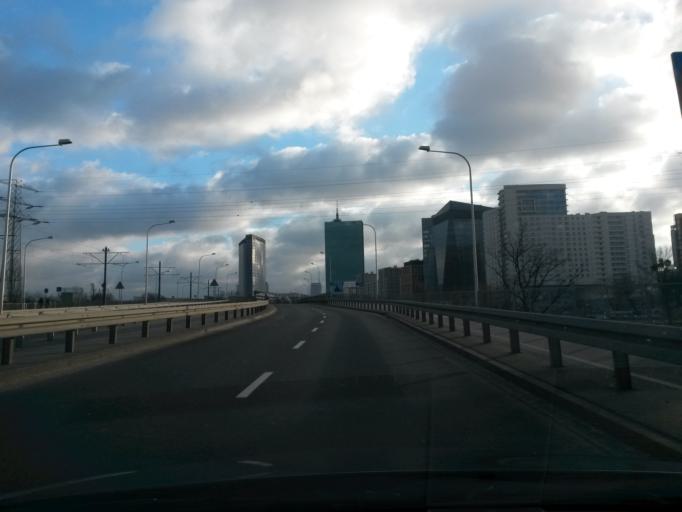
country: PL
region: Masovian Voivodeship
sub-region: Warszawa
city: Zoliborz
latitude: 52.2604
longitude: 20.9944
